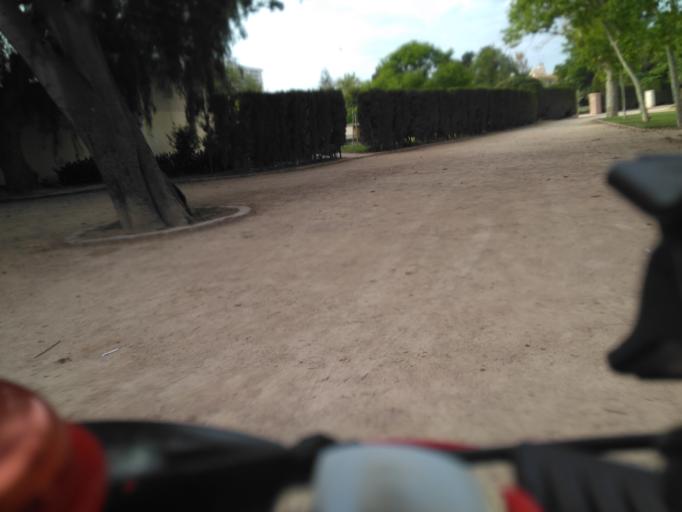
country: ES
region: Valencia
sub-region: Provincia de Valencia
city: Valencia
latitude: 39.4811
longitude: -0.3674
